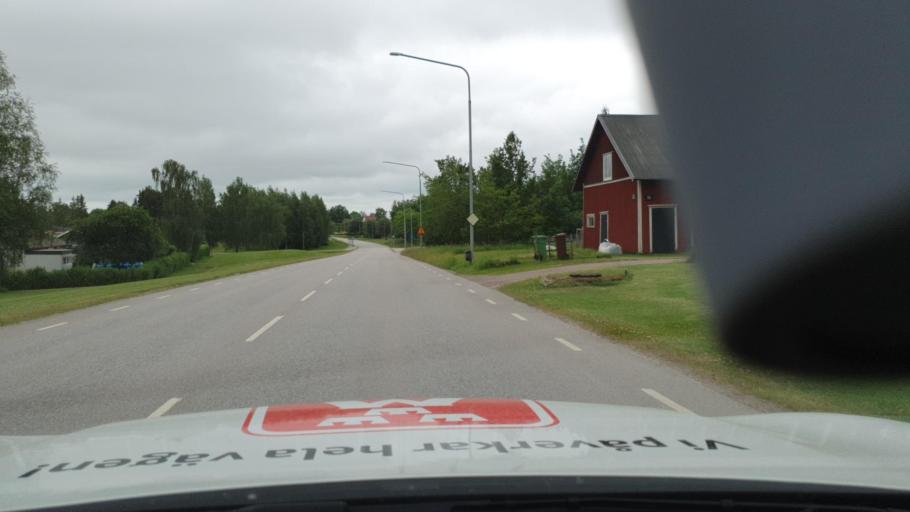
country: SE
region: Vaestra Goetaland
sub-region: Tibro Kommun
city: Tibro
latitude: 58.4079
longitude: 14.1518
